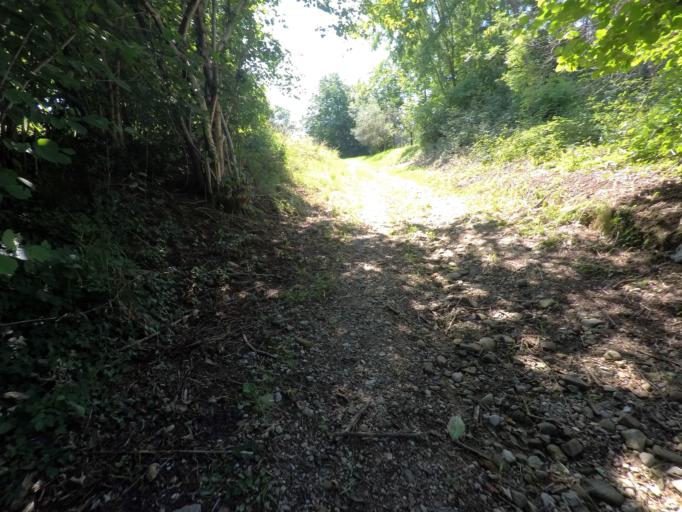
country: IT
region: Friuli Venezia Giulia
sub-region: Provincia di Udine
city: Tarcento
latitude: 46.1970
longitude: 13.2235
